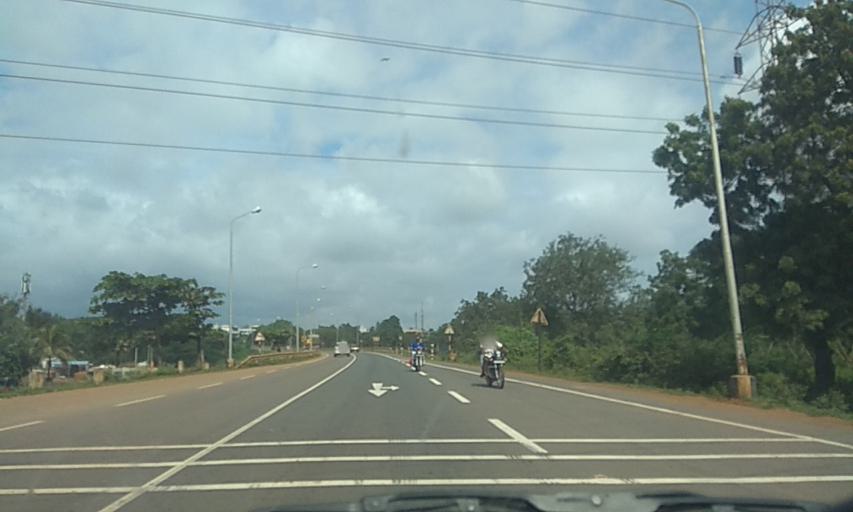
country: IN
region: Karnataka
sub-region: Dharwad
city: Hubli
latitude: 15.3284
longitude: 75.1202
